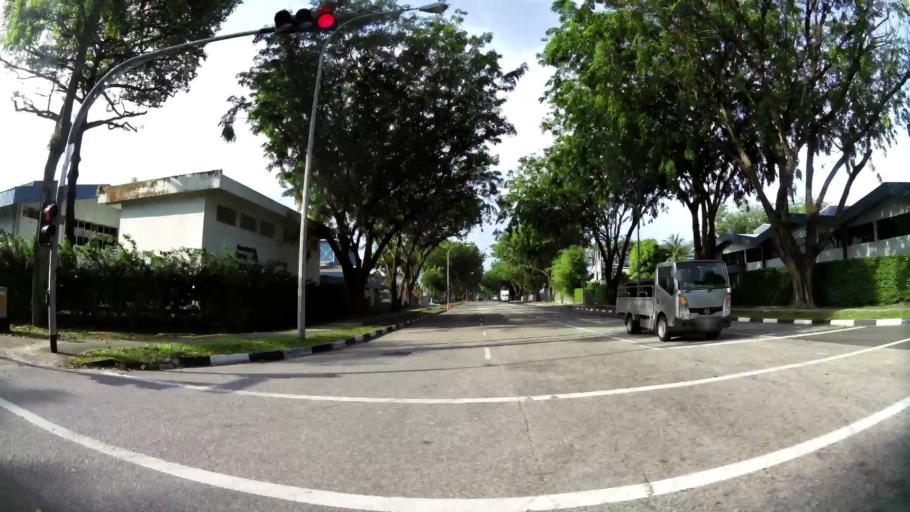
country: MY
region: Johor
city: Johor Bahru
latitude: 1.3266
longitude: 103.6557
